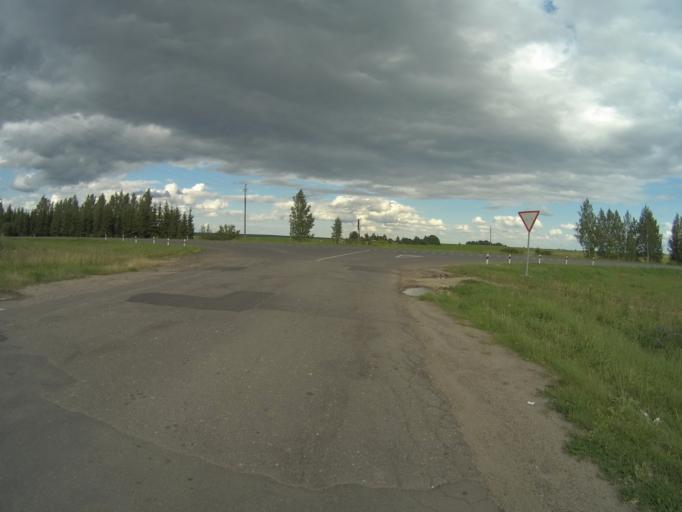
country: RU
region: Vladimir
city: Suzdal'
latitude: 56.3420
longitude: 40.4742
